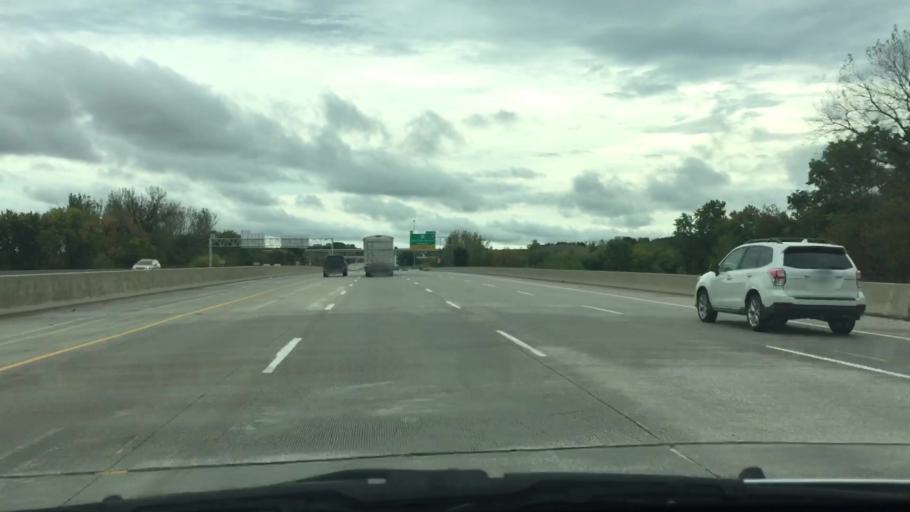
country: US
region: Iowa
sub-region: Polk County
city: West Des Moines
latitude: 41.5340
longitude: -93.7744
